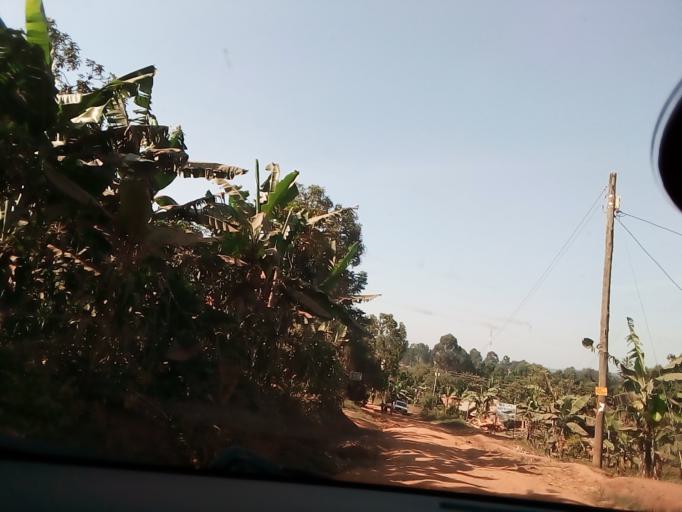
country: UG
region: Central Region
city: Masaka
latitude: -0.3383
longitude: 31.7304
